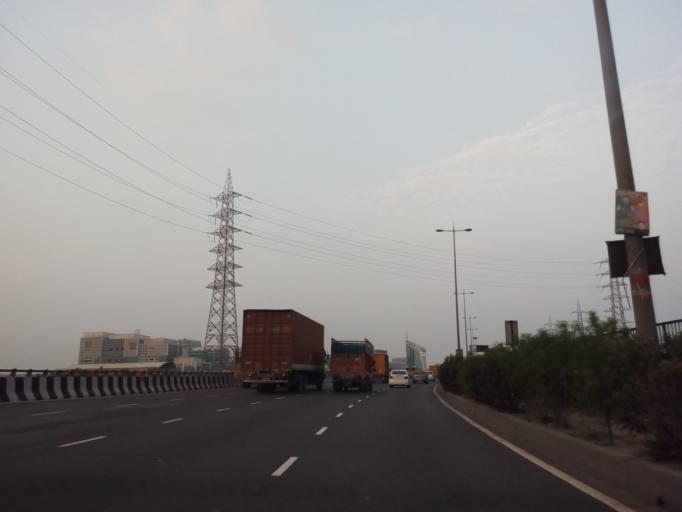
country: IN
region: Haryana
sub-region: Gurgaon
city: Gurgaon
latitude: 28.5051
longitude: 77.0947
